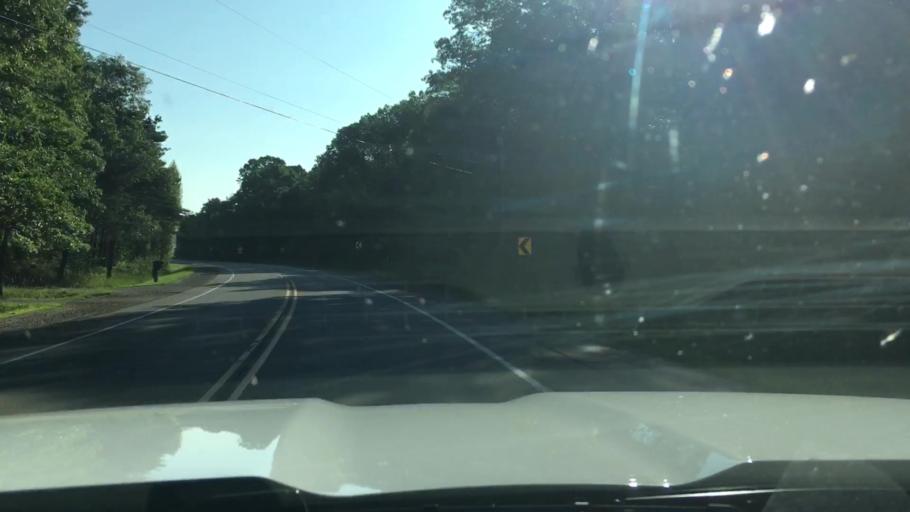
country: US
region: Michigan
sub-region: Kent County
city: Lowell
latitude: 42.9075
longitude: -85.3558
